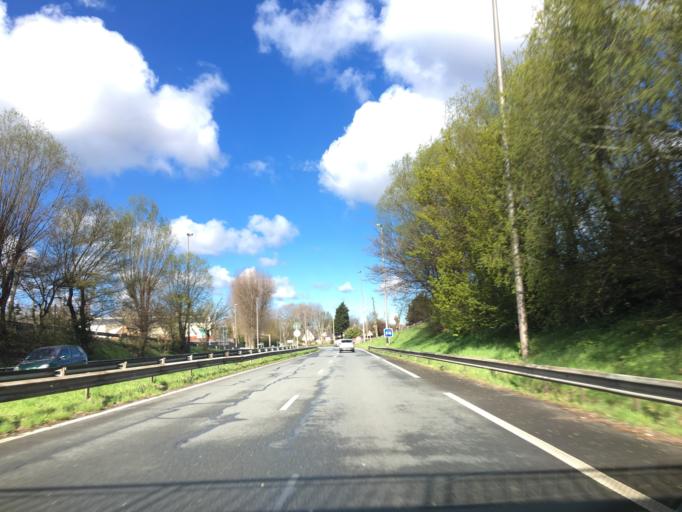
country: FR
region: Nord-Pas-de-Calais
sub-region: Departement du Nord
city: Saint-Pol-sur-Mer
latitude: 51.0228
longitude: 2.3317
